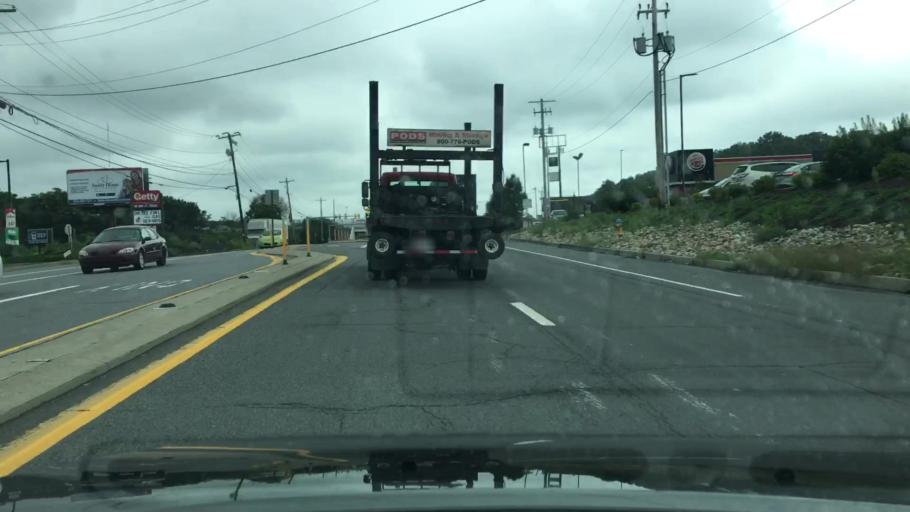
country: US
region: Pennsylvania
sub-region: Luzerne County
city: Dupont
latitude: 41.3147
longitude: -75.7557
